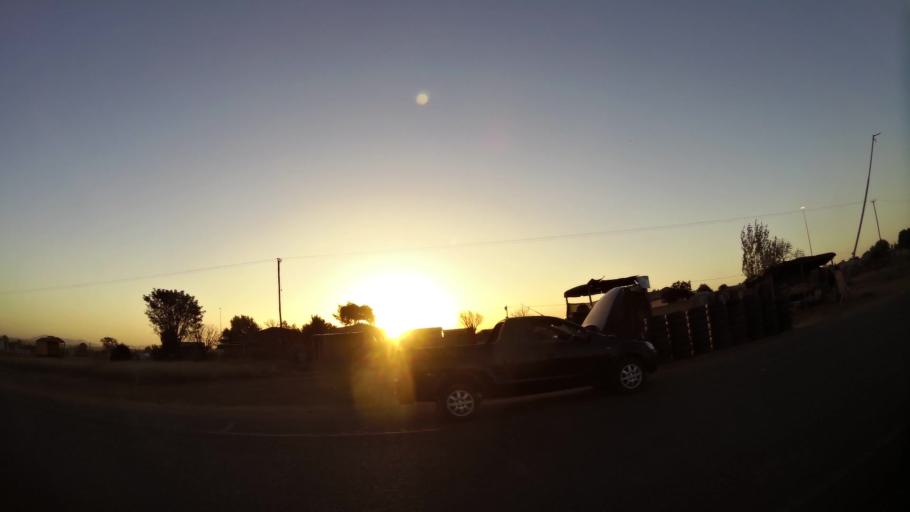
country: ZA
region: North-West
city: Ga-Rankuwa
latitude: -25.5696
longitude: 28.0536
